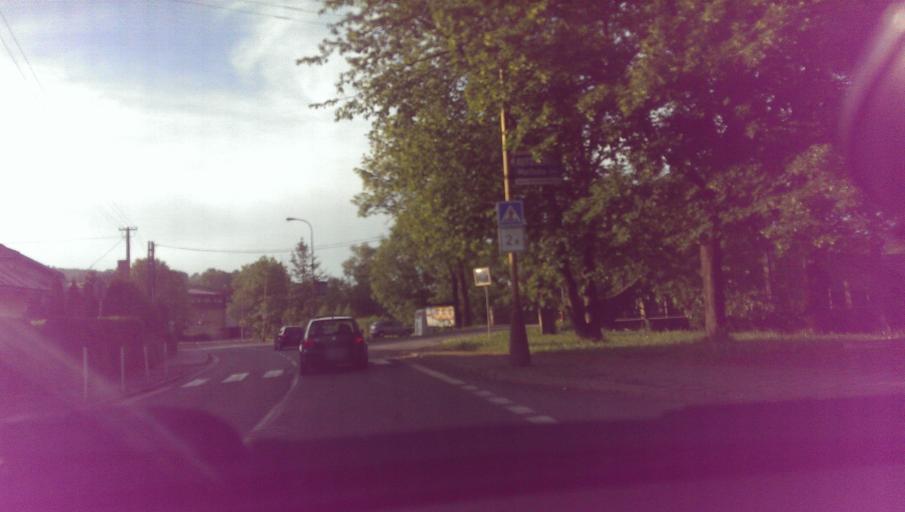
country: CZ
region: Zlin
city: Valasska Polanka
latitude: 49.2566
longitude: 17.9968
